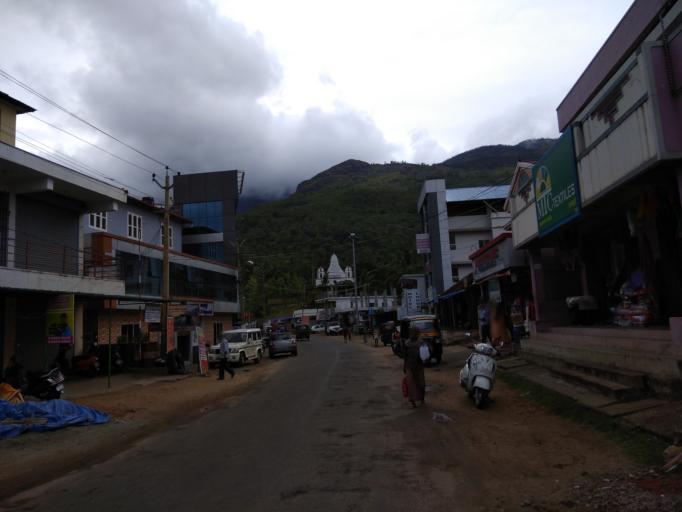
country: IN
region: Kerala
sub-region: Idukki
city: Munnar
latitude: 10.2763
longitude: 77.1625
